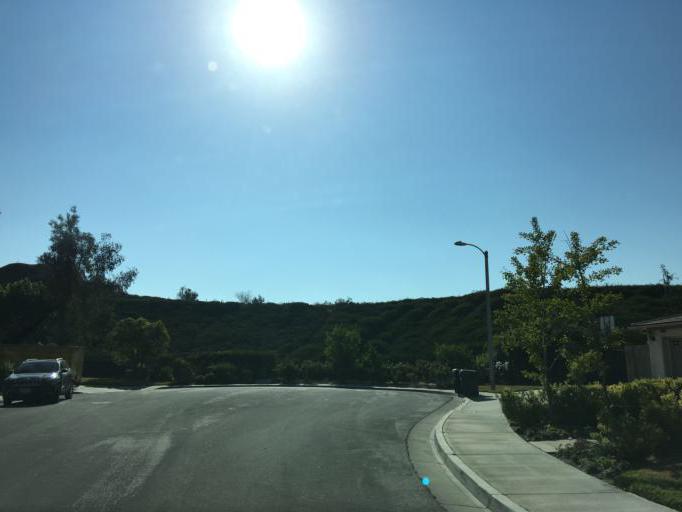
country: US
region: California
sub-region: Los Angeles County
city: Santa Clarita
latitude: 34.3764
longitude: -118.5817
